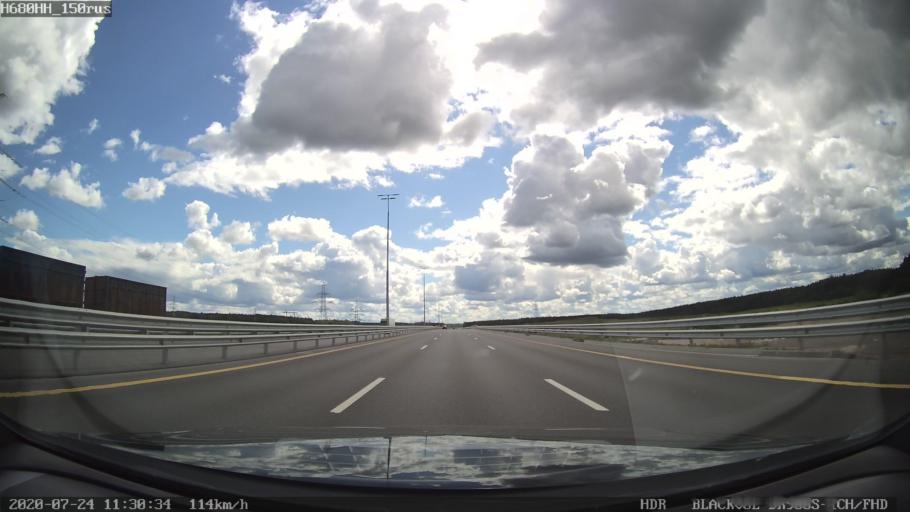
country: RU
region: Leningrad
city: Krasnyy Bor
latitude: 59.6651
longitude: 30.6193
